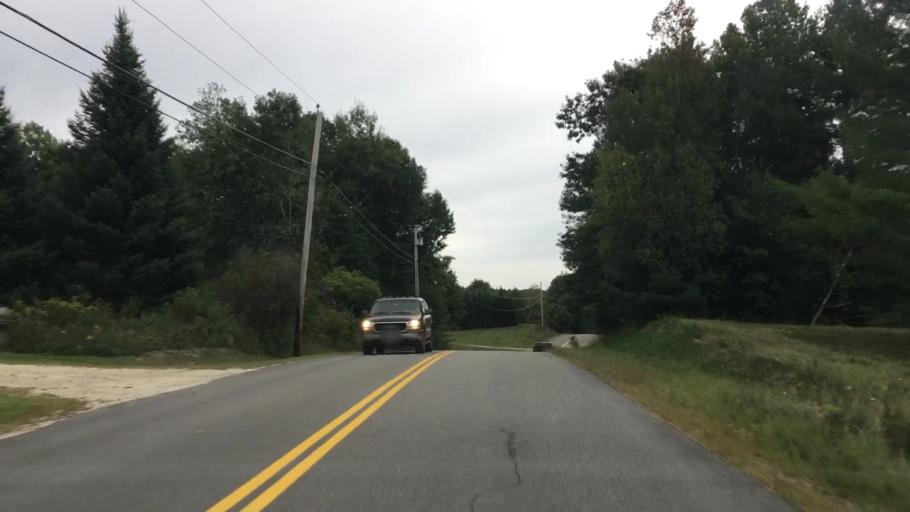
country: US
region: Maine
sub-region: Cumberland County
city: New Gloucester
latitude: 43.9201
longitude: -70.2481
